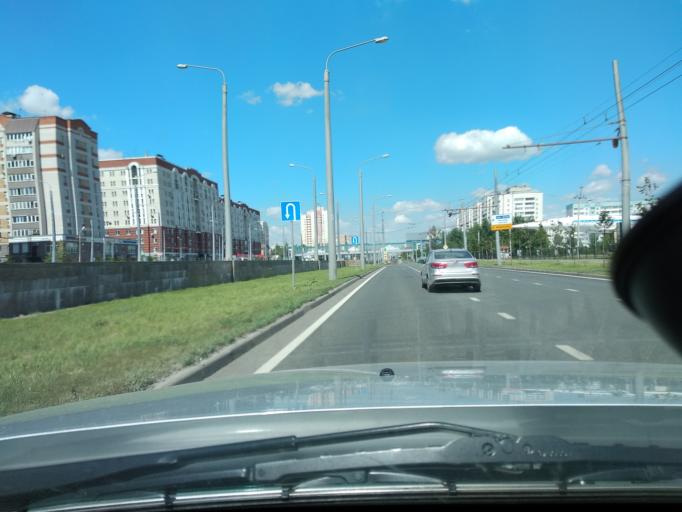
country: RU
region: Tatarstan
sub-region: Gorod Kazan'
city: Kazan
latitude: 55.8206
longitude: 49.1340
